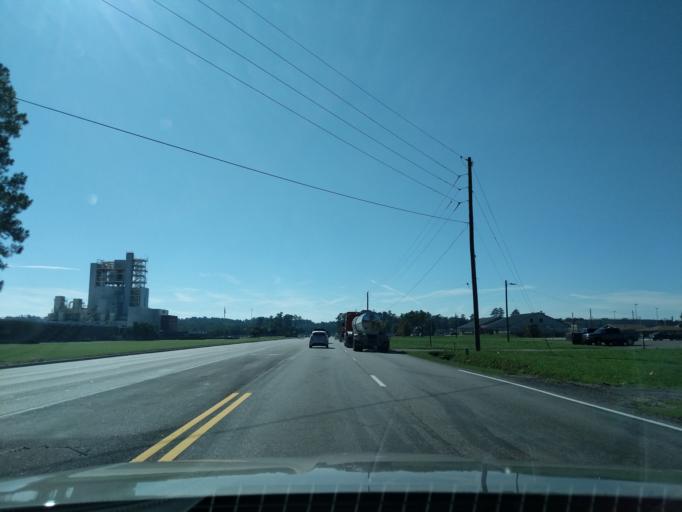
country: US
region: Georgia
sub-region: Richmond County
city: Augusta
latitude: 33.3942
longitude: -82.0053
